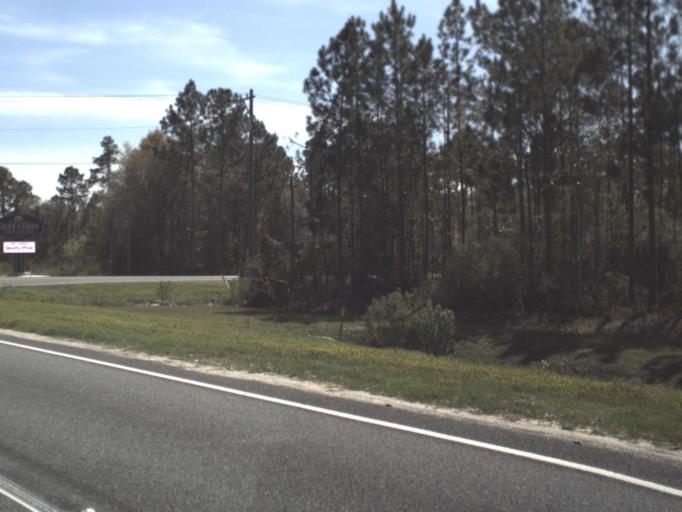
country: US
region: Florida
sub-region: Bay County
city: Lynn Haven
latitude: 30.3031
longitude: -85.6487
